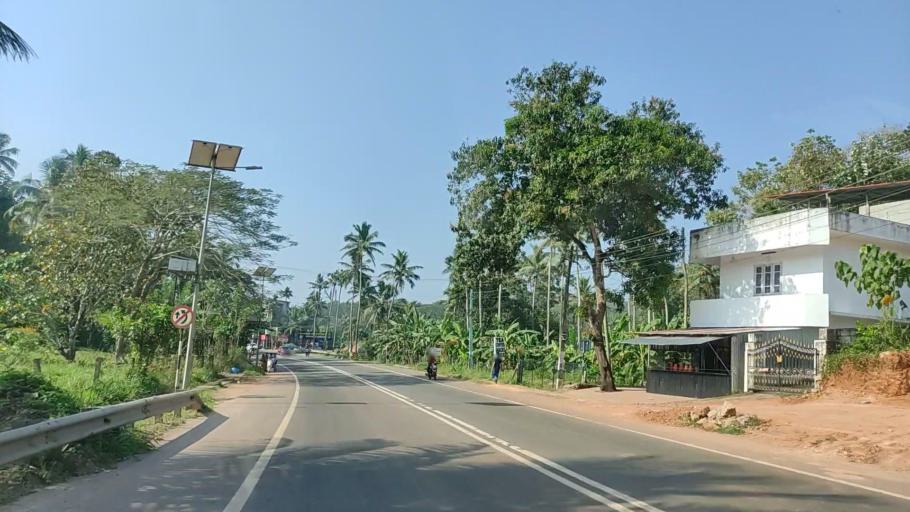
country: IN
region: Kerala
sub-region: Kollam
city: Punalur
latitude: 8.8813
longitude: 76.8680
